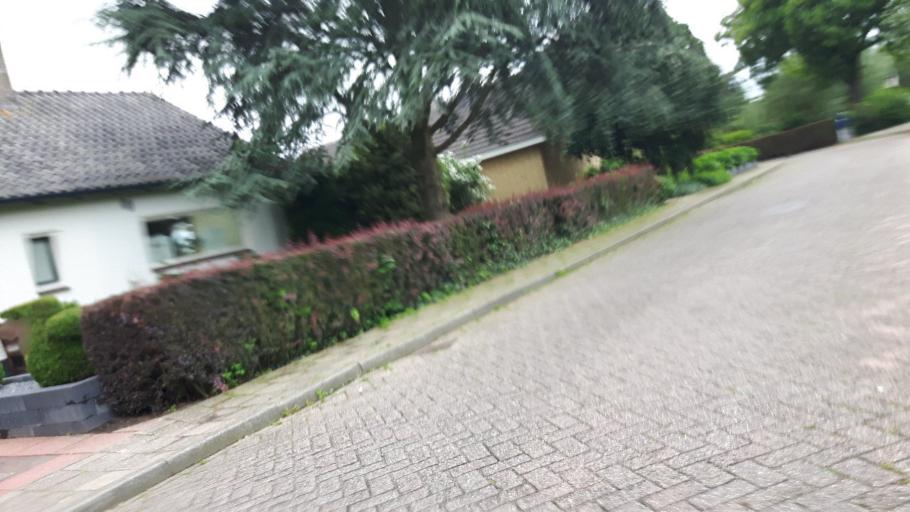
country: NL
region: Utrecht
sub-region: Gemeente Woerden
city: Woerden
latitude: 52.0760
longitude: 4.8212
